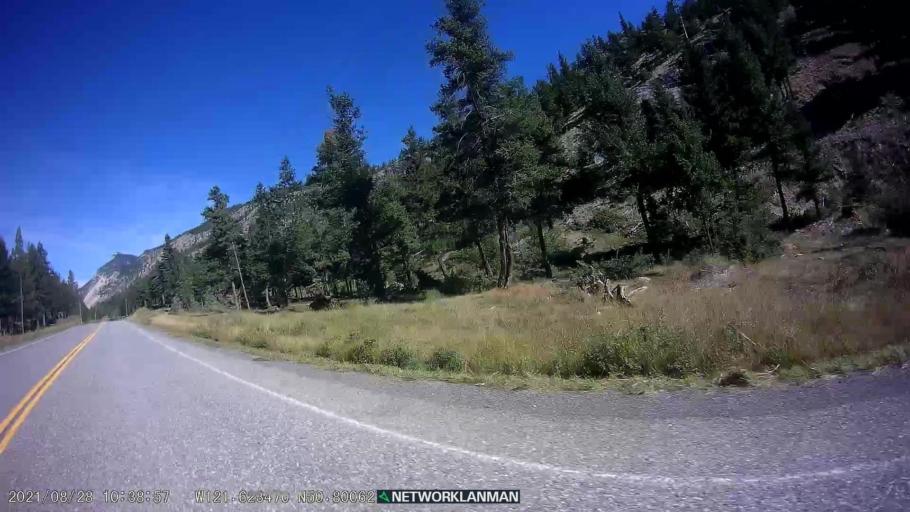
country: CA
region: British Columbia
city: Cache Creek
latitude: 50.8004
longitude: -121.6248
